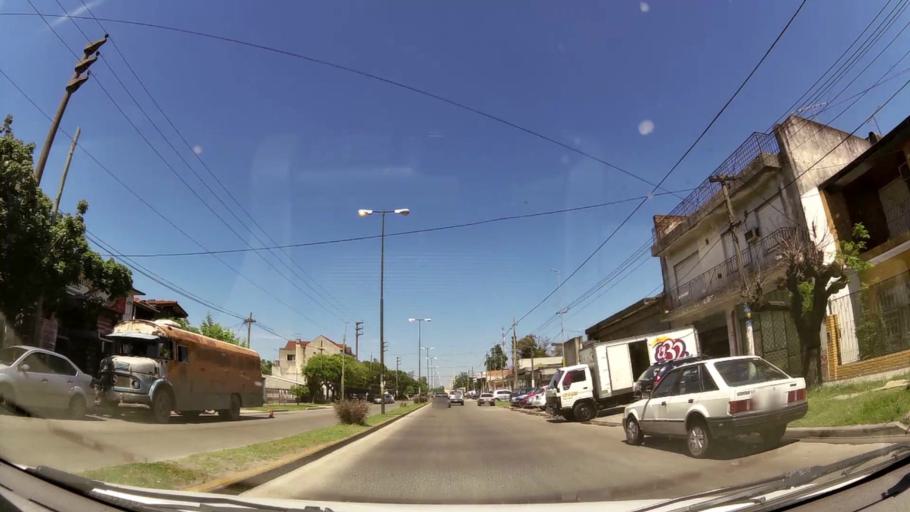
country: AR
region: Buenos Aires
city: Ituzaingo
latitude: -34.6776
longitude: -58.6683
